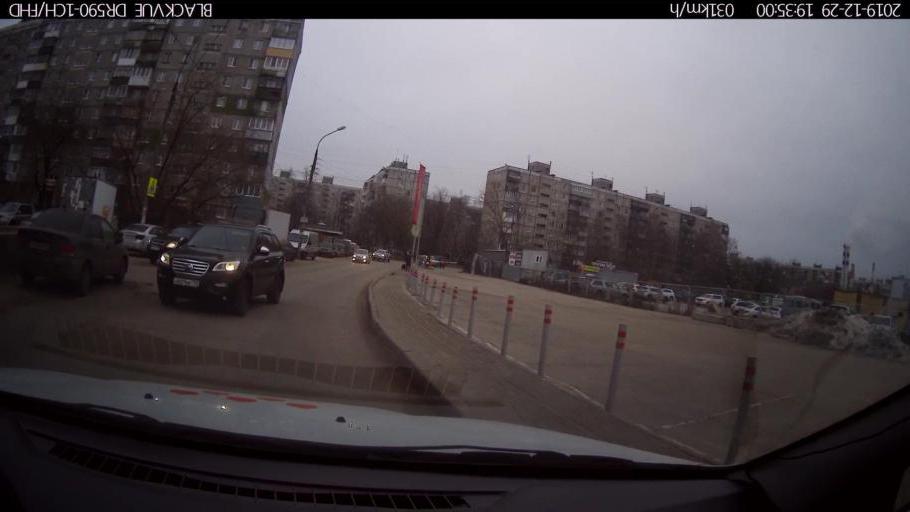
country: RU
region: Nizjnij Novgorod
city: Neklyudovo
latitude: 56.3514
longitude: 43.8599
